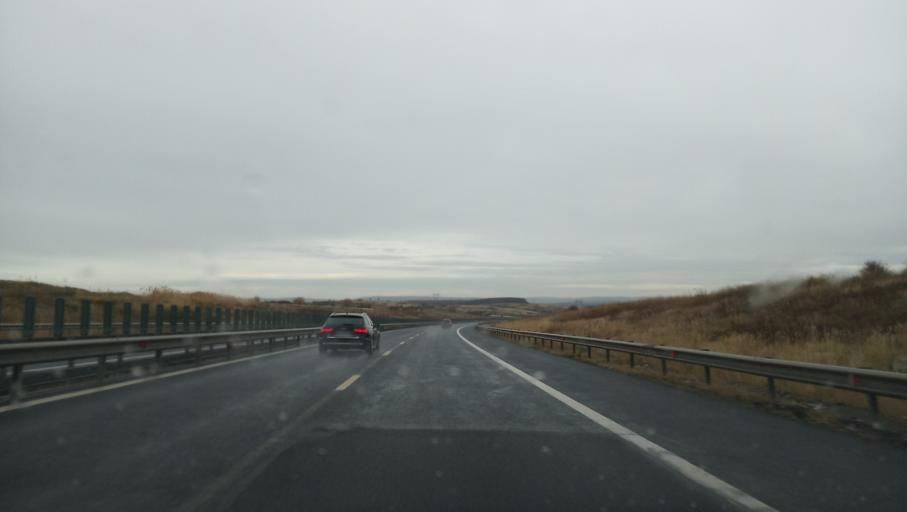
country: RO
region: Sibiu
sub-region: Comuna Apoldu de Jos
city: Apoldu de Jos
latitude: 45.8352
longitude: 23.8625
